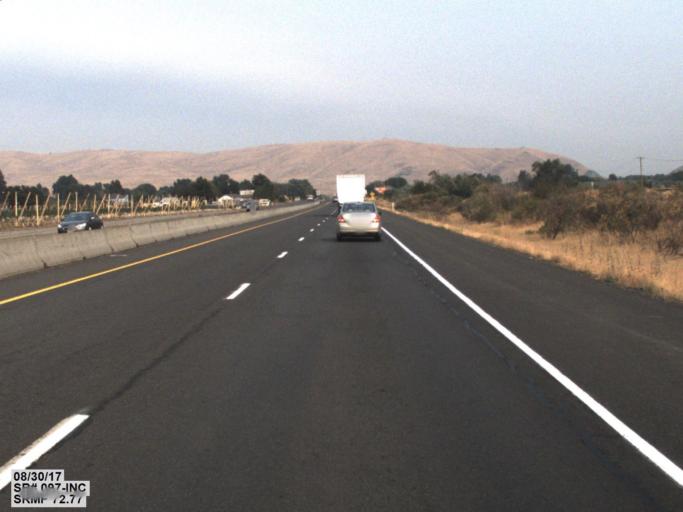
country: US
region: Washington
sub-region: Yakima County
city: Union Gap
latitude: 46.4959
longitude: -120.4611
